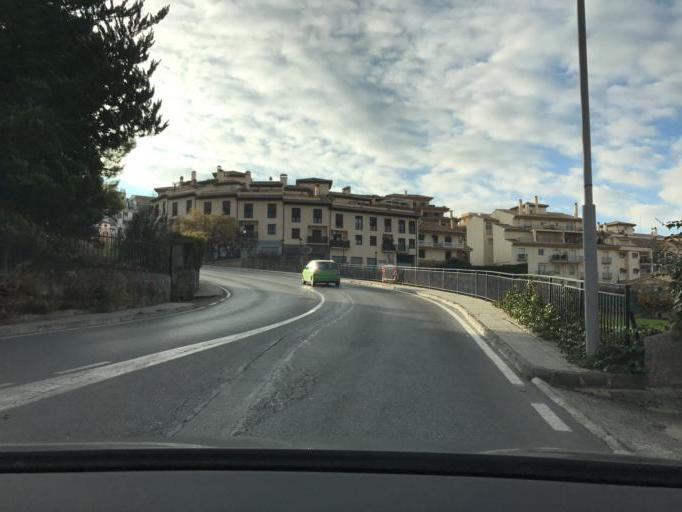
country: ES
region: Andalusia
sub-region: Provincia de Granada
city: Cajar
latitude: 37.1360
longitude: -3.5592
